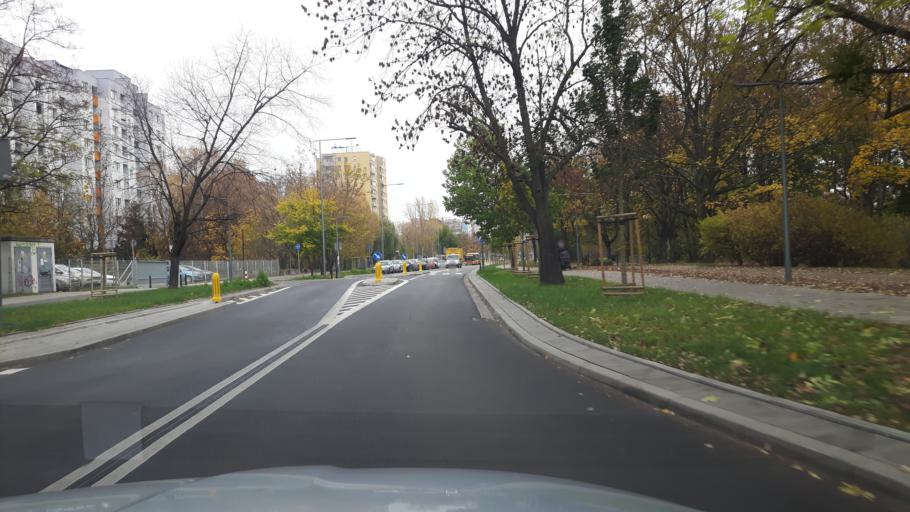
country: PL
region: Masovian Voivodeship
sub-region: Warszawa
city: Targowek
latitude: 52.2742
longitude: 21.0503
